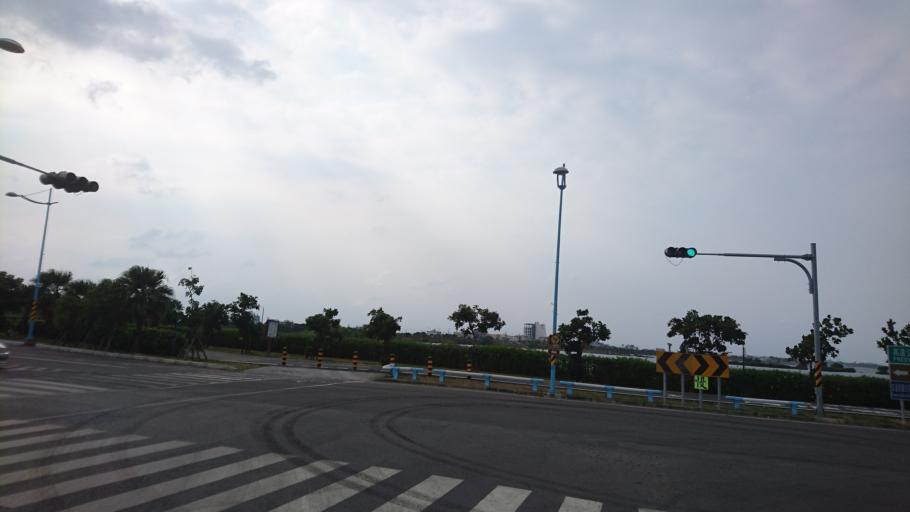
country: TW
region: Taiwan
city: Fengshan
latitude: 22.4332
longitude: 120.4893
